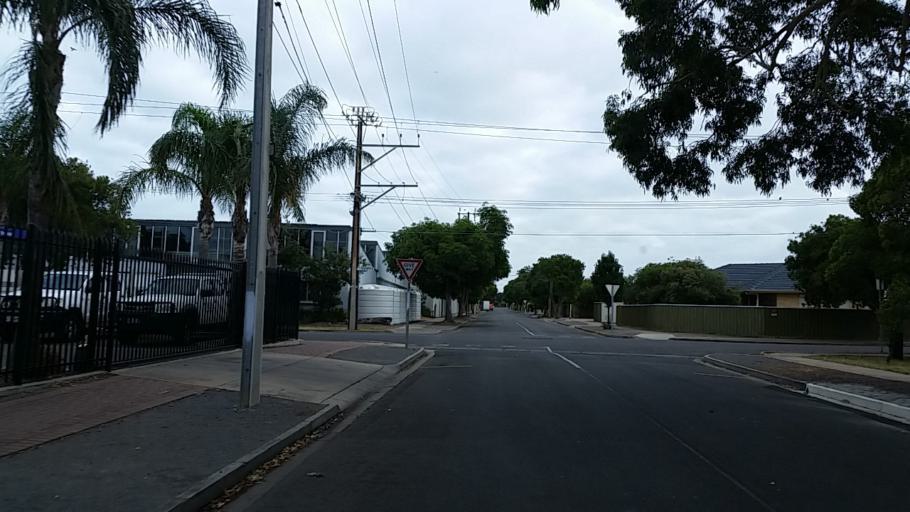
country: AU
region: South Australia
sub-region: Holdfast Bay
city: North Brighton
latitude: -35.0013
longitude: 138.5245
